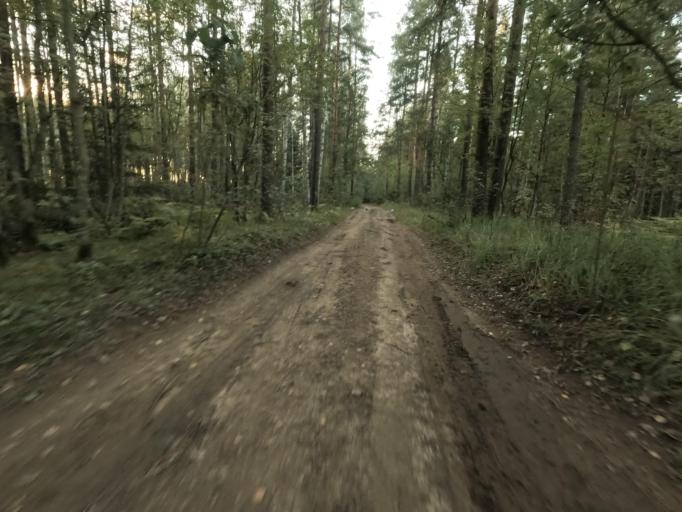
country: RU
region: Leningrad
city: Otradnoye
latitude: 59.8387
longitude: 30.8047
